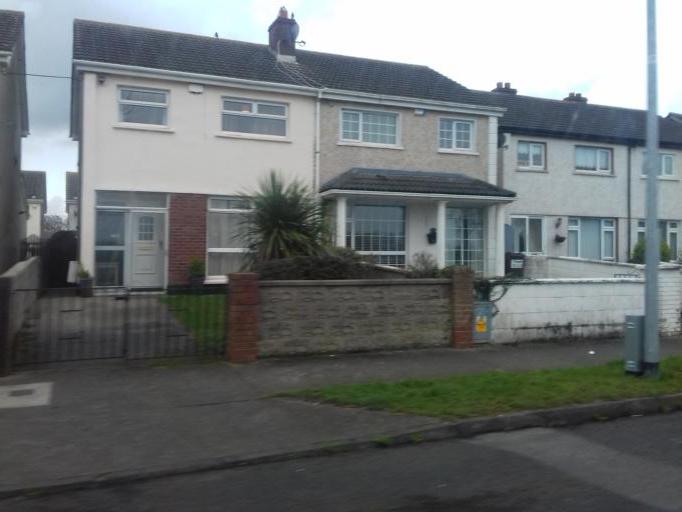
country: IE
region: Leinster
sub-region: Fingal County
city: Blanchardstown
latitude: 53.3949
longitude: -6.3816
